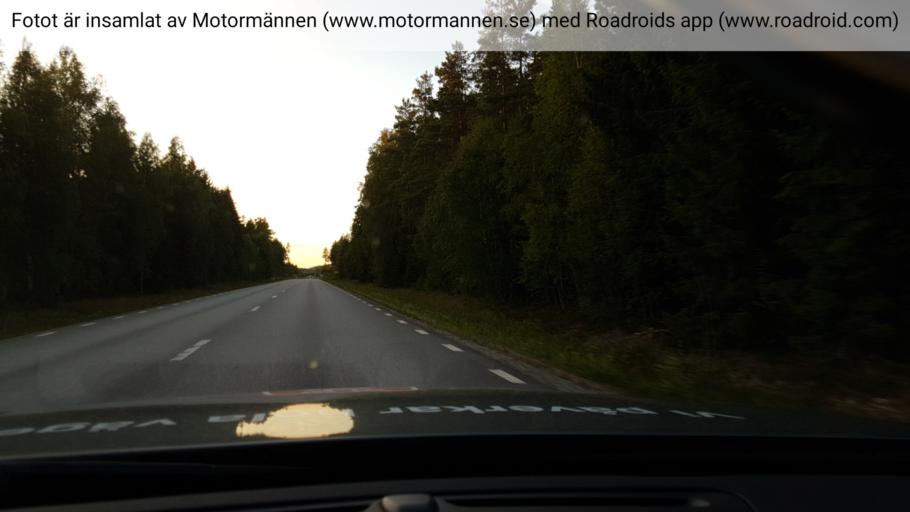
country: SE
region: OErebro
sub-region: Karlskoga Kommun
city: Karlskoga
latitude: 59.4173
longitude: 14.5168
